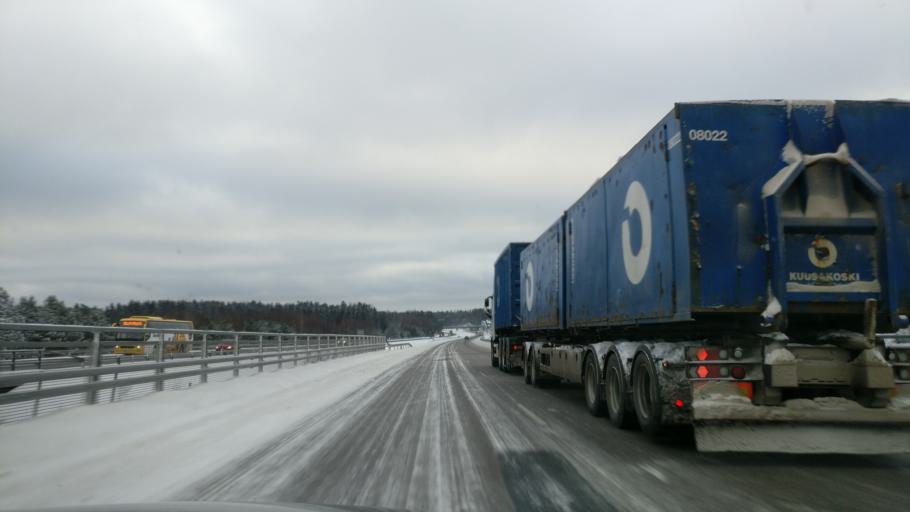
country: FI
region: Paijanne Tavastia
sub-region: Lahti
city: Nastola
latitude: 61.1015
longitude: 25.9096
